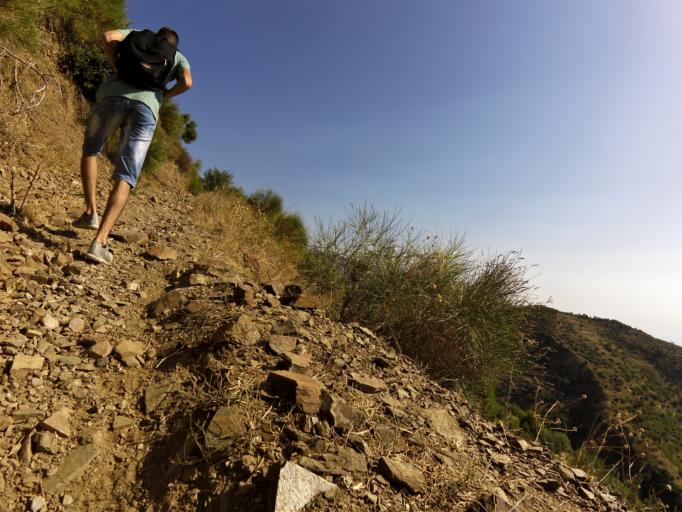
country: IT
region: Calabria
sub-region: Provincia di Reggio Calabria
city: Bivongi
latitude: 38.4970
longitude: 16.4542
